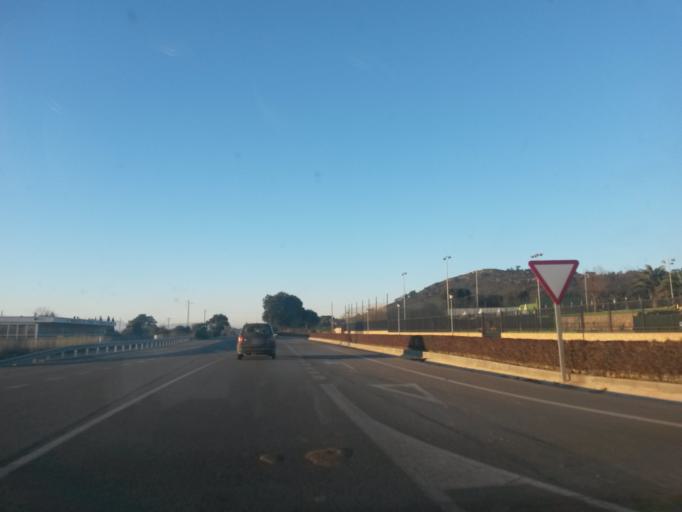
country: ES
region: Catalonia
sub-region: Provincia de Girona
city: Regencos
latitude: 41.9553
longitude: 3.1575
